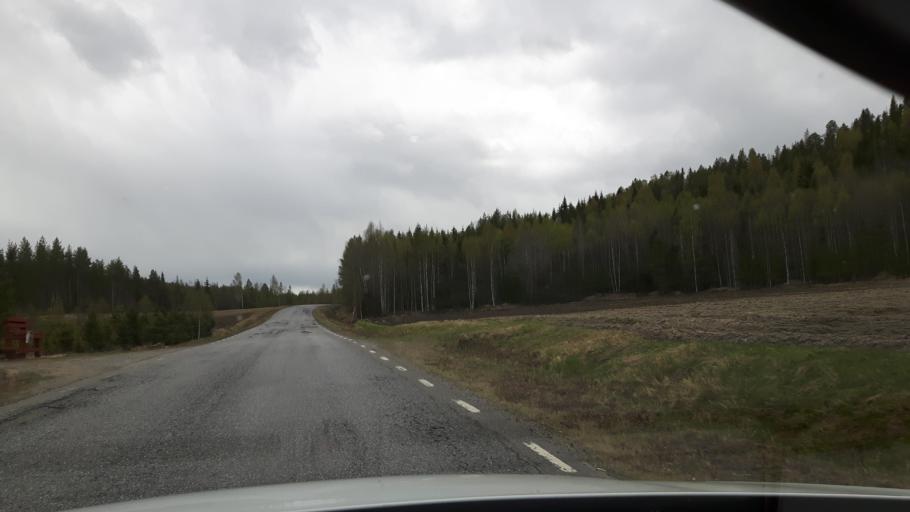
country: SE
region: Vaesterbotten
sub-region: Skelleftea Kommun
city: Burtraesk
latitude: 64.2884
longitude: 20.5255
